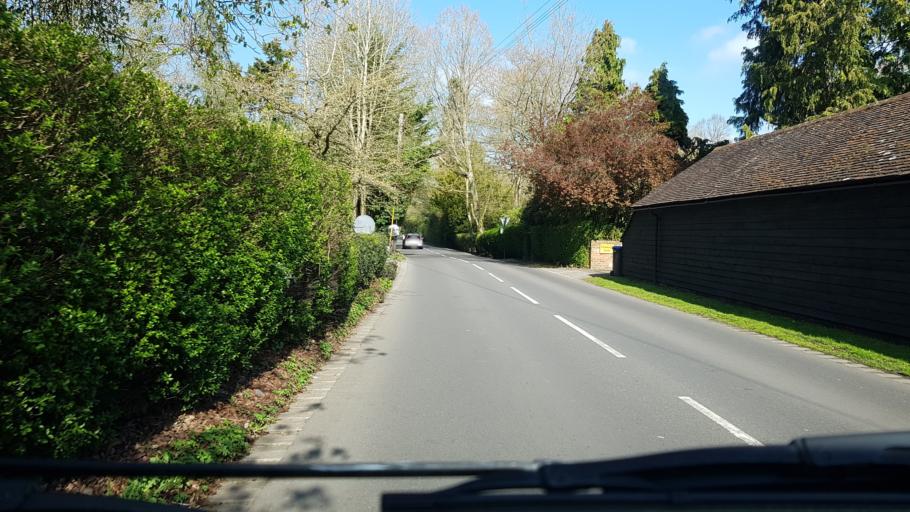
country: GB
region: England
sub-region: Surrey
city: Knaphill
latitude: 51.2939
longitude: -0.6003
